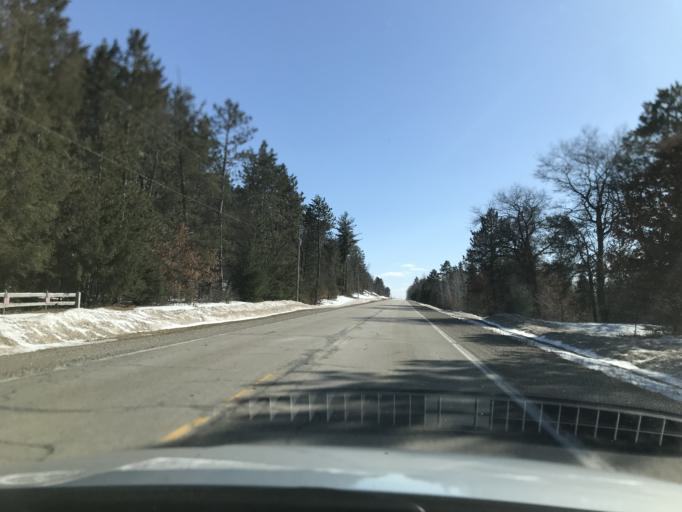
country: US
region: Wisconsin
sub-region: Marinette County
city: Niagara
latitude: 45.3627
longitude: -88.1007
